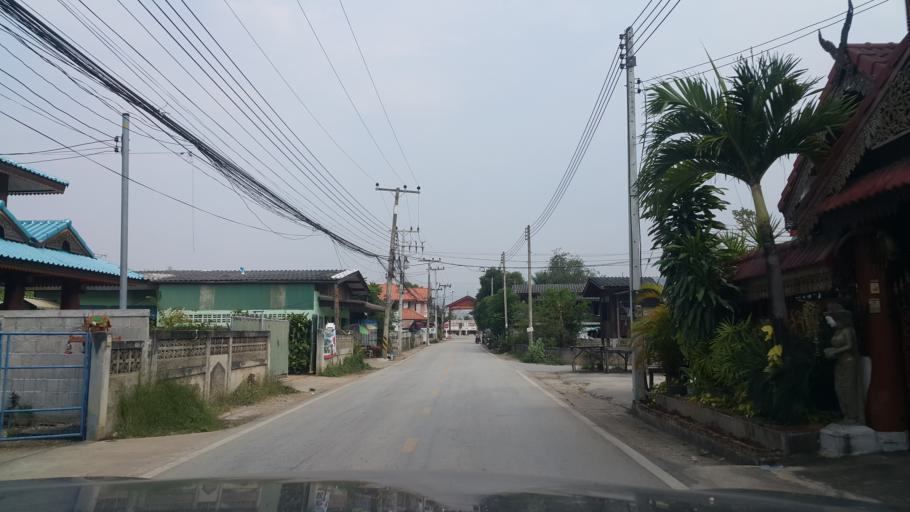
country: TH
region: Lampang
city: Sop Prap
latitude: 17.8875
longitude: 99.3375
